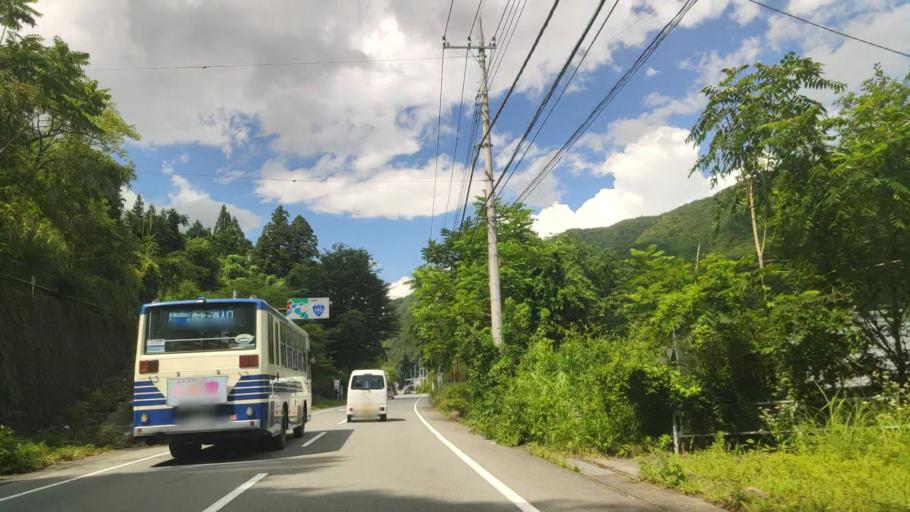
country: JP
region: Yamanashi
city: Enzan
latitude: 35.7706
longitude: 138.7371
